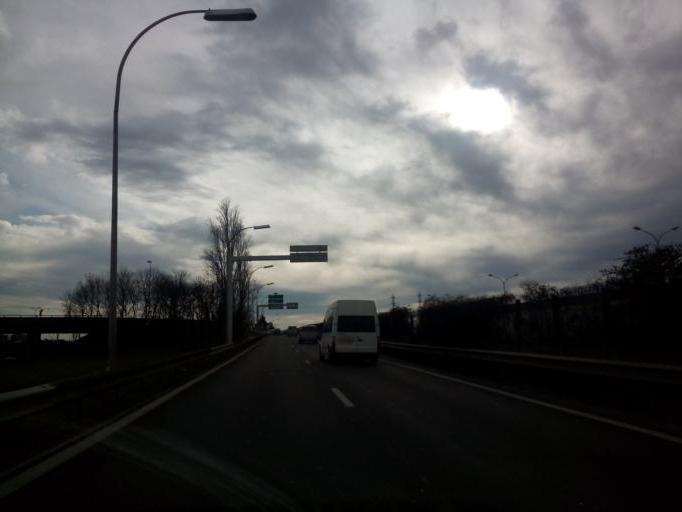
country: FR
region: Rhone-Alpes
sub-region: Departement du Rhone
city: Saint-Fons
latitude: 45.7170
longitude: 4.8423
